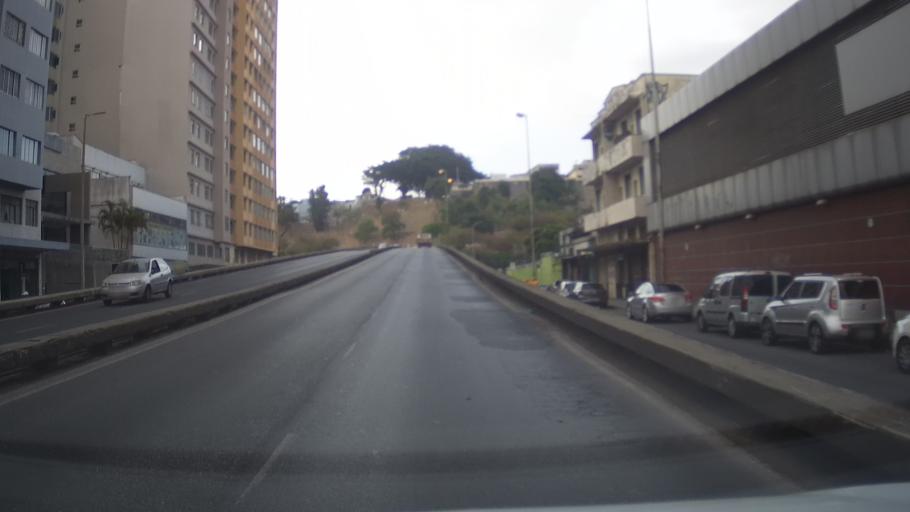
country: BR
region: Minas Gerais
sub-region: Belo Horizonte
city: Belo Horizonte
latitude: -19.9194
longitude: -43.9471
